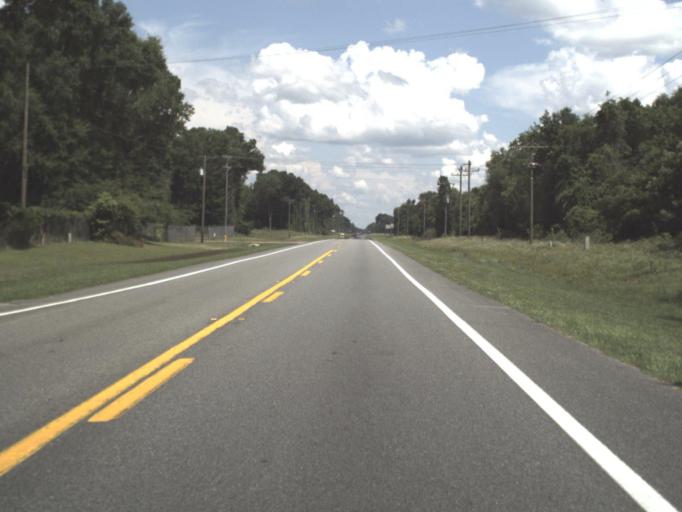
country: US
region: Florida
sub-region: Alachua County
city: High Springs
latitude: 29.9155
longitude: -82.7065
